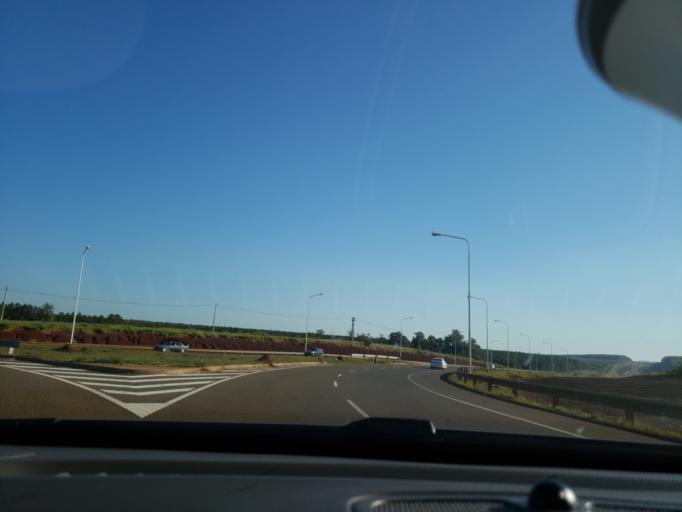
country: AR
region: Misiones
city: Garupa
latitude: -27.4652
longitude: -55.9195
